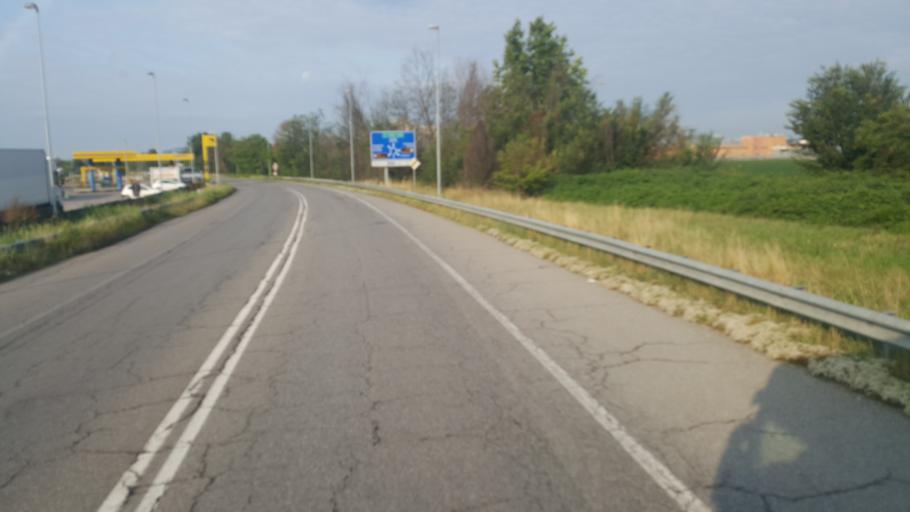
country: IT
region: Lombardy
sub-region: Provincia di Brescia
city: Bassano Bresciano
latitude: 45.3172
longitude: 10.1200
